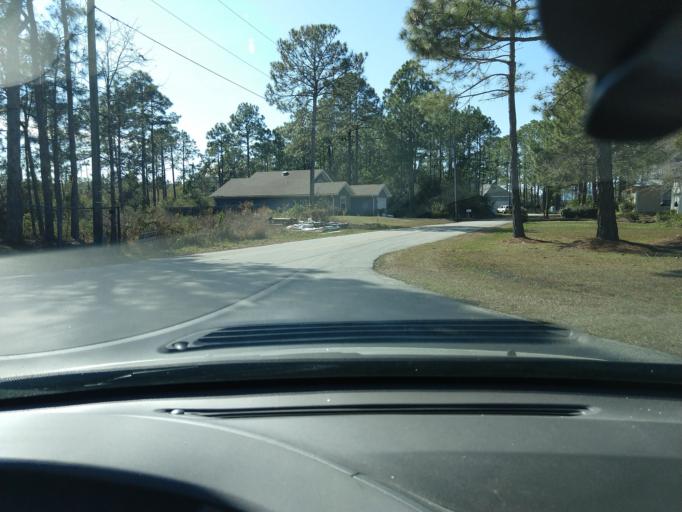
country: US
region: Florida
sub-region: Walton County
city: Miramar Beach
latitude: 30.3790
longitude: -86.3012
